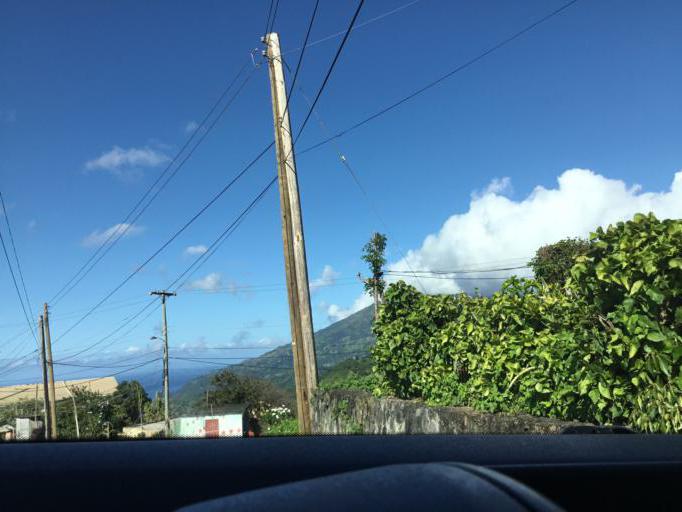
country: VC
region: Saint David
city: Chateaubelair
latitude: 13.2705
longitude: -61.2413
